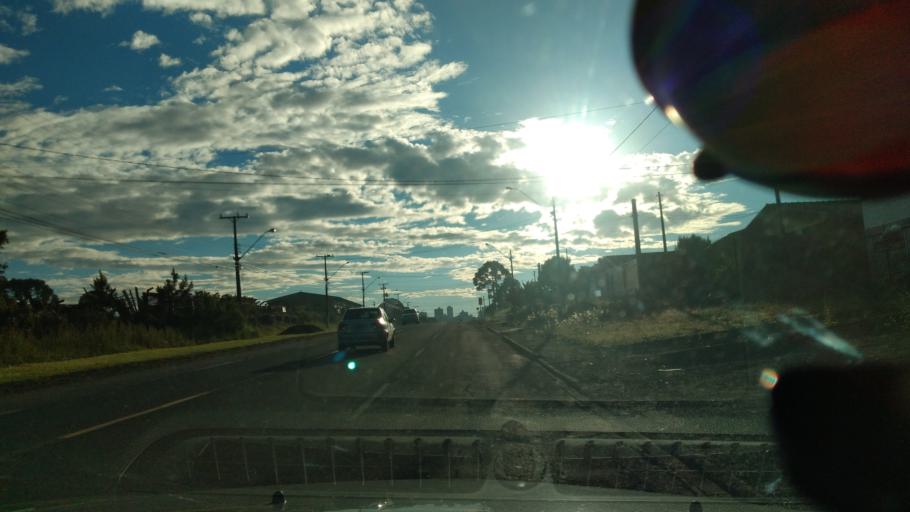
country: BR
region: Parana
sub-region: Guarapuava
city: Guarapuava
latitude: -25.3937
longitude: -51.4905
